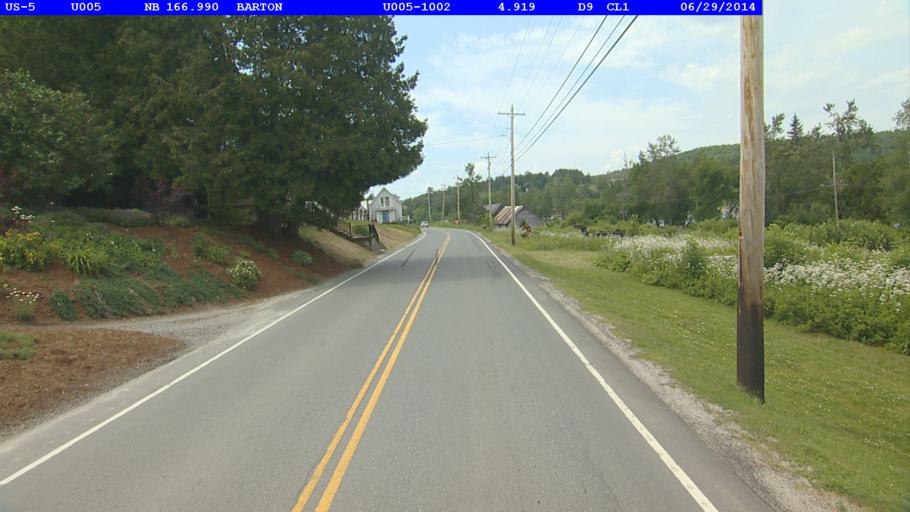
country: US
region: Vermont
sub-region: Orleans County
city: Newport
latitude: 44.7428
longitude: -72.1702
